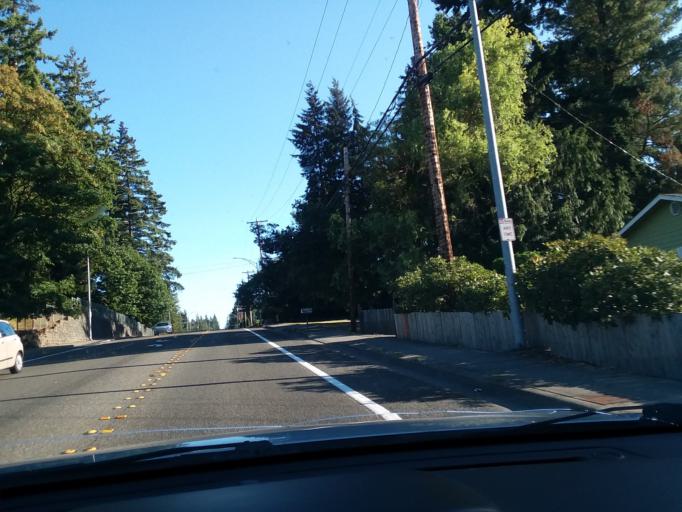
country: US
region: Washington
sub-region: Snohomish County
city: Lynnwood
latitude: 47.8134
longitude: -122.3033
